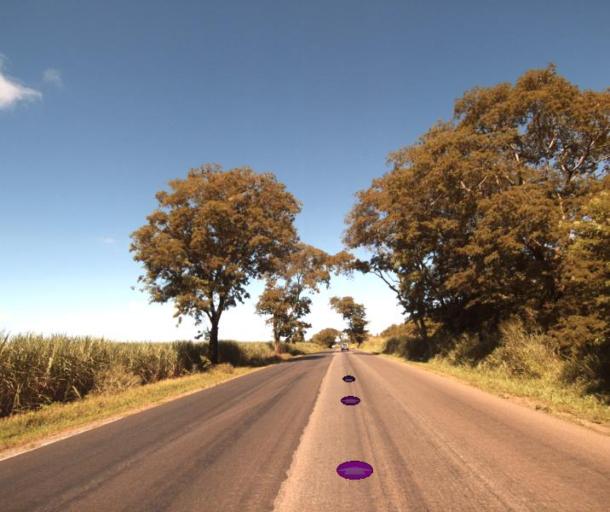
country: BR
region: Goias
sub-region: Itapaci
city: Itapaci
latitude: -15.1299
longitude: -49.5122
